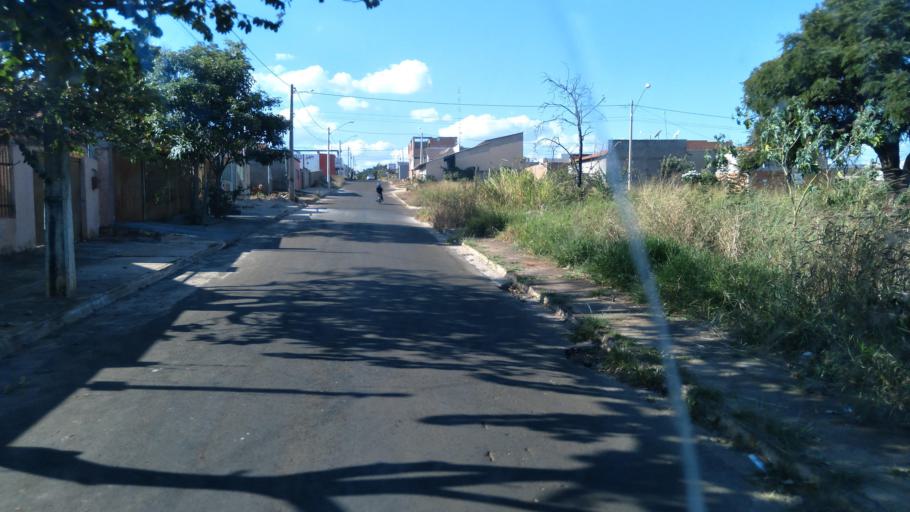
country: BR
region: Goias
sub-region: Mineiros
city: Mineiros
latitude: -17.5471
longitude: -52.5385
